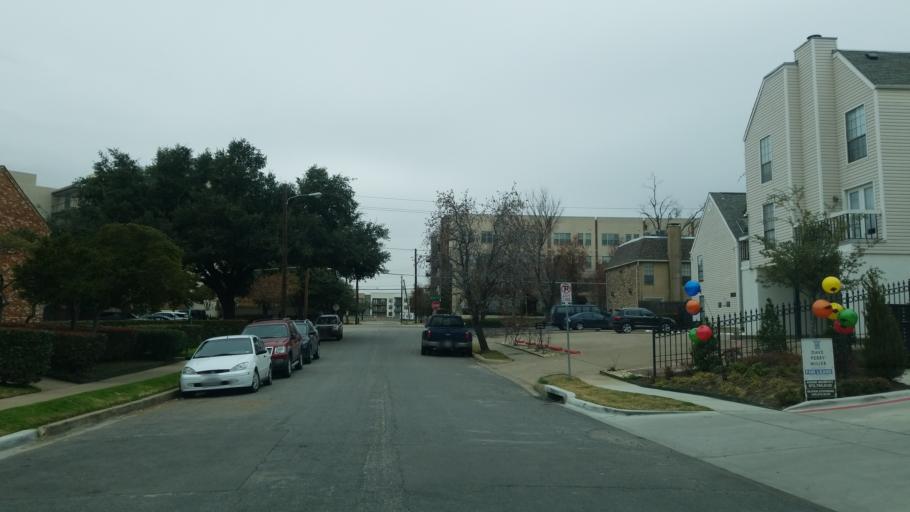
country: US
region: Texas
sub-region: Dallas County
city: Dallas
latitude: 32.8119
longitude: -96.8159
